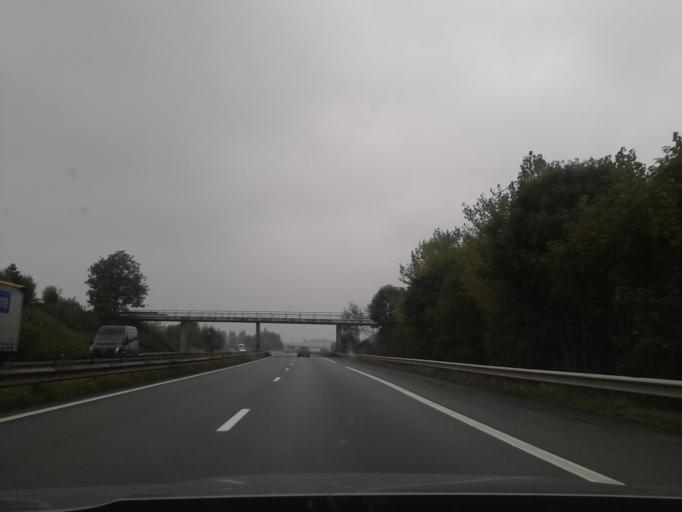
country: FR
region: Nord-Pas-de-Calais
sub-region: Departement du Nord
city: Lieu-Saint-Amand
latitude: 50.2781
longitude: 3.3406
